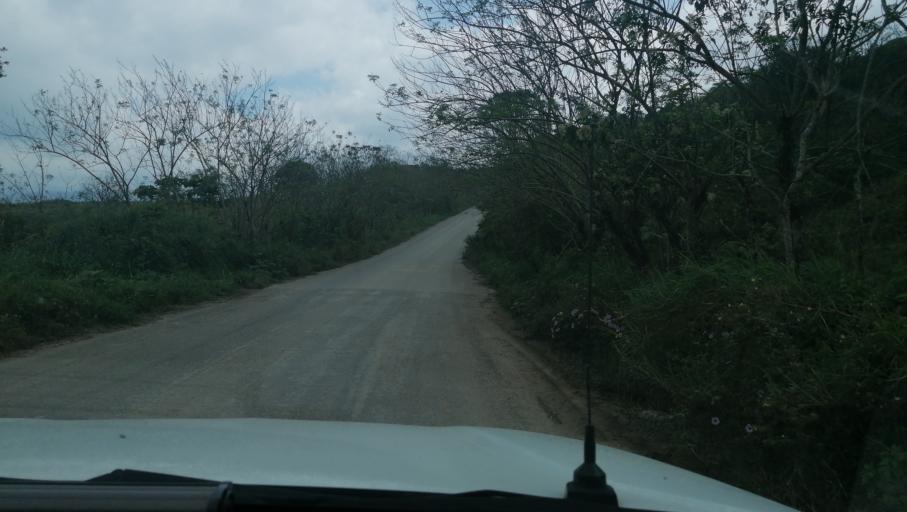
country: MX
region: Chiapas
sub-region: Ocotepec
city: San Pablo Huacano
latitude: 17.2692
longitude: -93.2634
